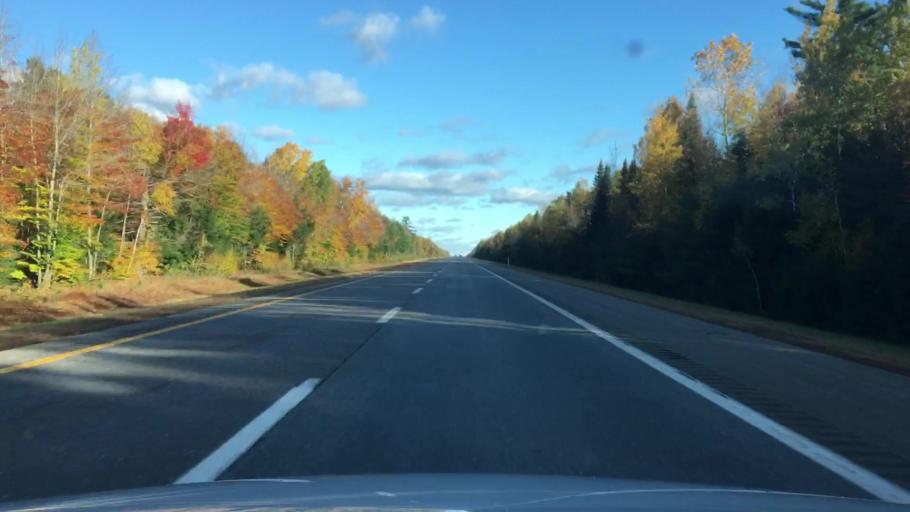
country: US
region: Maine
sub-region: Penobscot County
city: Greenbush
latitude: 45.0694
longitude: -68.6901
